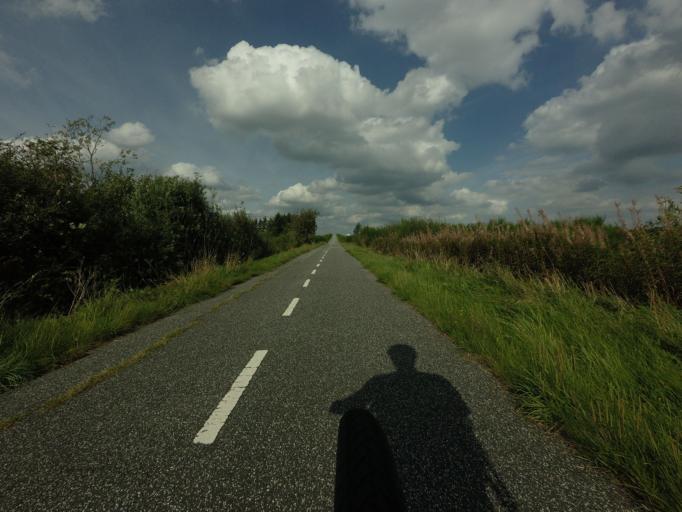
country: DK
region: Central Jutland
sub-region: Herning Kommune
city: Sunds
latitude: 56.1871
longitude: 9.0095
